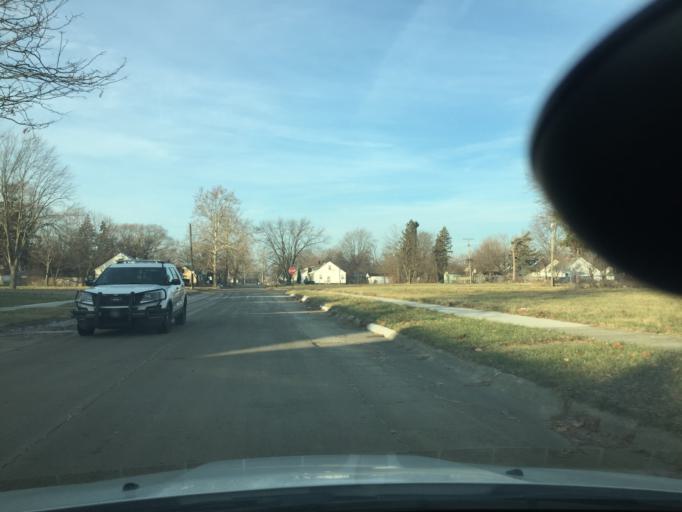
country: US
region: Michigan
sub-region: Macomb County
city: Eastpointe
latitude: 42.4392
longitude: -82.9549
